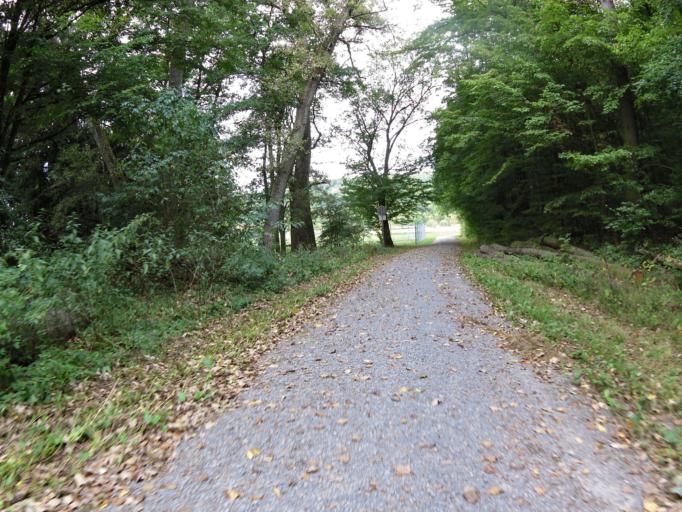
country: DE
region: Bavaria
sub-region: Regierungsbezirk Unterfranken
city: Waldbrunn
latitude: 49.7737
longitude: 9.7973
